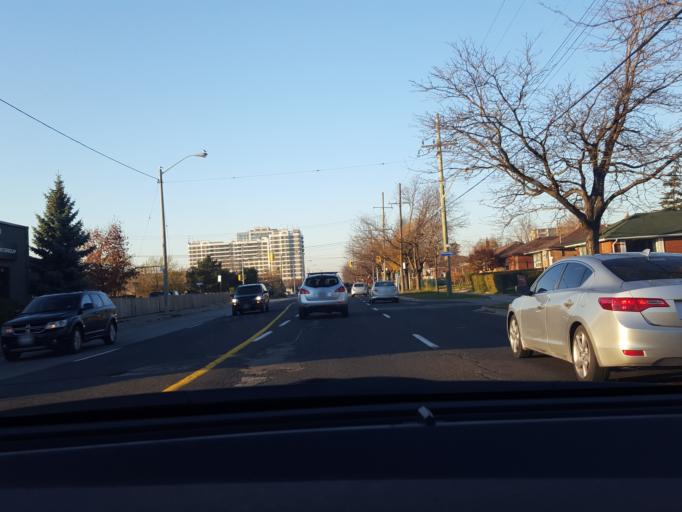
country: CA
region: Ontario
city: Scarborough
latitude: 43.7432
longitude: -79.2830
